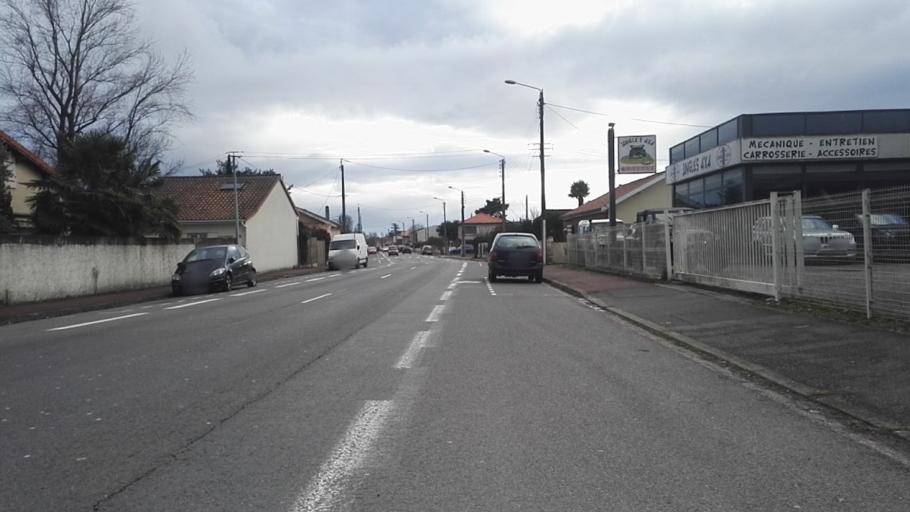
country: FR
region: Aquitaine
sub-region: Departement de la Gironde
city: Eysines
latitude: 44.8598
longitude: -0.6430
